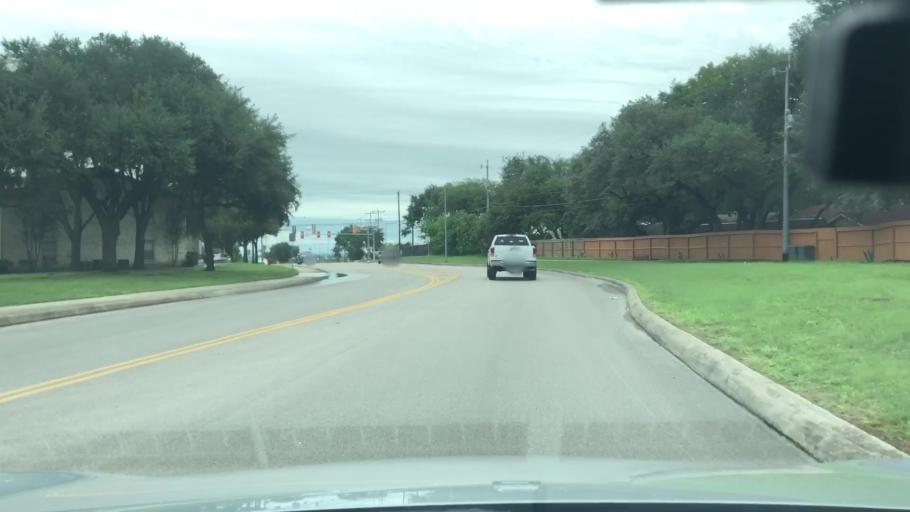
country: US
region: Texas
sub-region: Bexar County
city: Universal City
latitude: 29.5515
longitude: -98.3091
